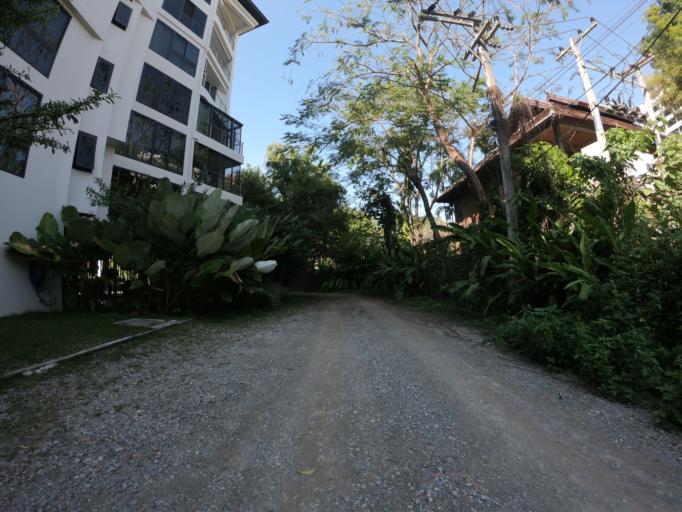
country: TH
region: Chiang Mai
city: Chiang Mai
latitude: 18.7794
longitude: 99.0013
